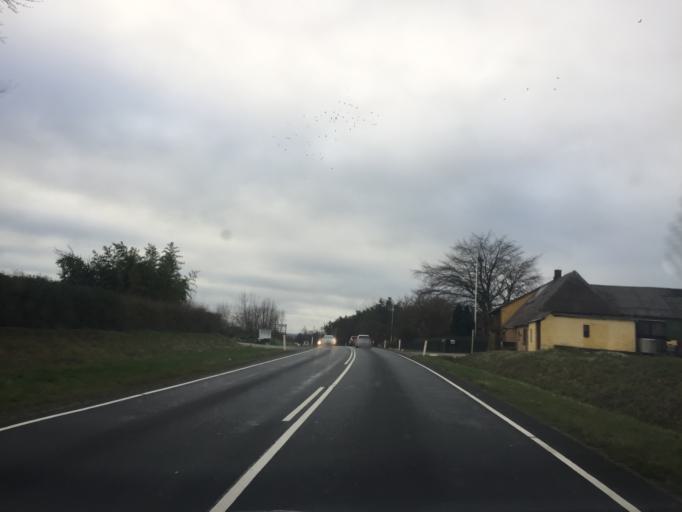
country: DK
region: South Denmark
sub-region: Nyborg Kommune
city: Nyborg
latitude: 55.2447
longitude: 10.7474
